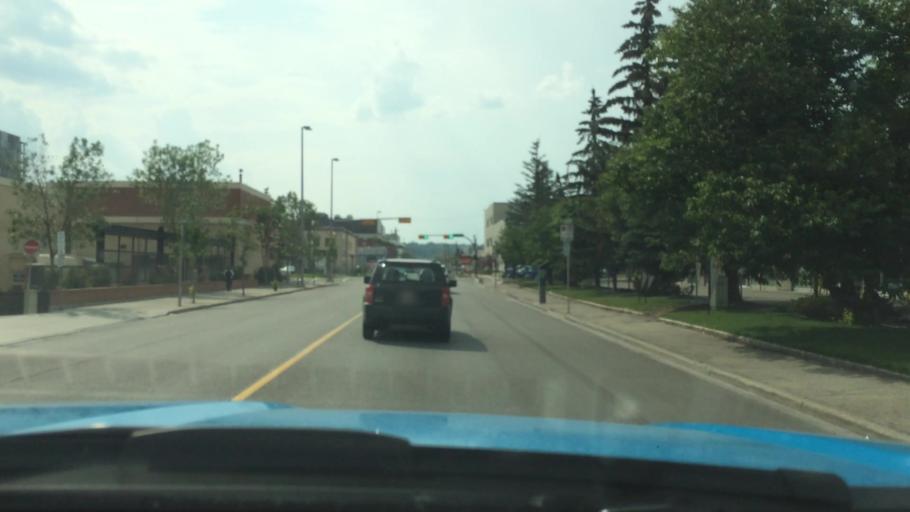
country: CA
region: Alberta
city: Calgary
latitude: 51.0440
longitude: -114.0873
